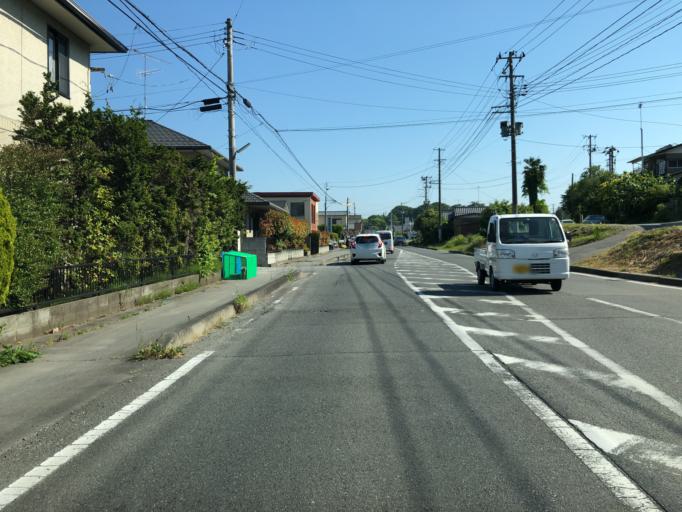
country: JP
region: Fukushima
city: Iwaki
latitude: 36.9938
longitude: 140.8540
